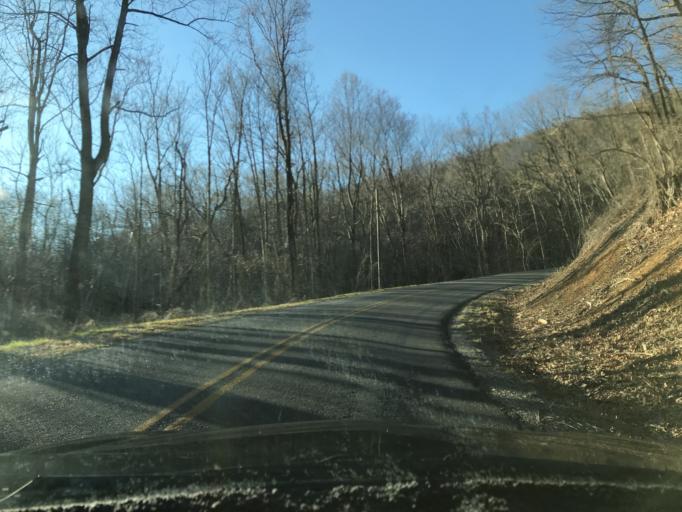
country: US
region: Virginia
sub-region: Botetourt County
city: Buchanan
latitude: 37.4764
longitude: -79.6579
